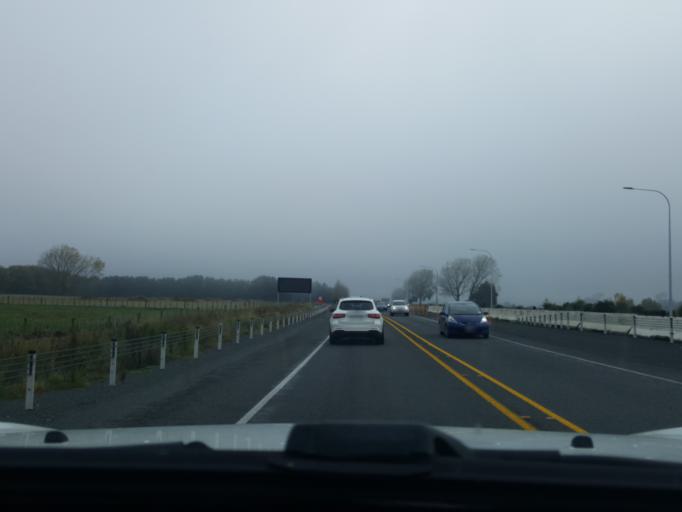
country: NZ
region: Waikato
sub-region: Waikato District
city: Te Kauwhata
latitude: -37.5028
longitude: 175.1648
